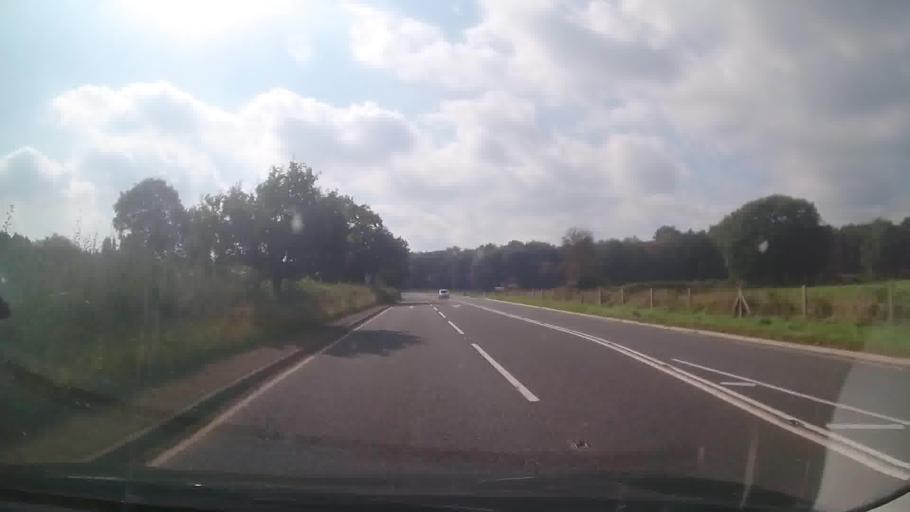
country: GB
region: England
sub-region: Cheshire West and Chester
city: Bickley
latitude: 53.0427
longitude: -2.6755
